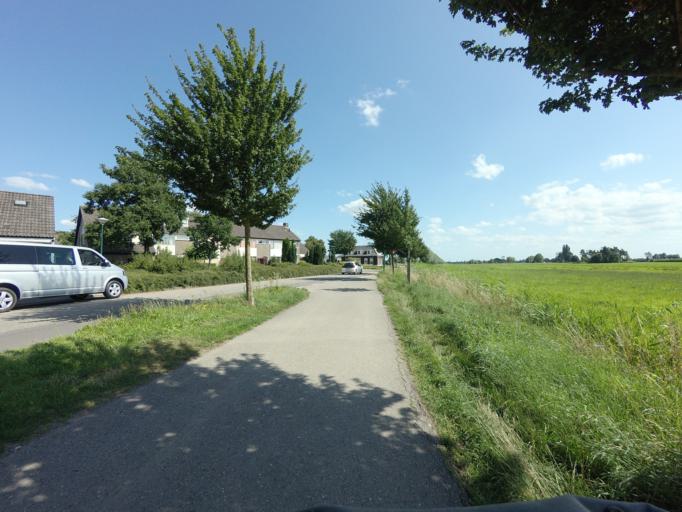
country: NL
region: Utrecht
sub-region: Gemeente Montfoort
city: Montfoort
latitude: 52.0357
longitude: 4.9502
